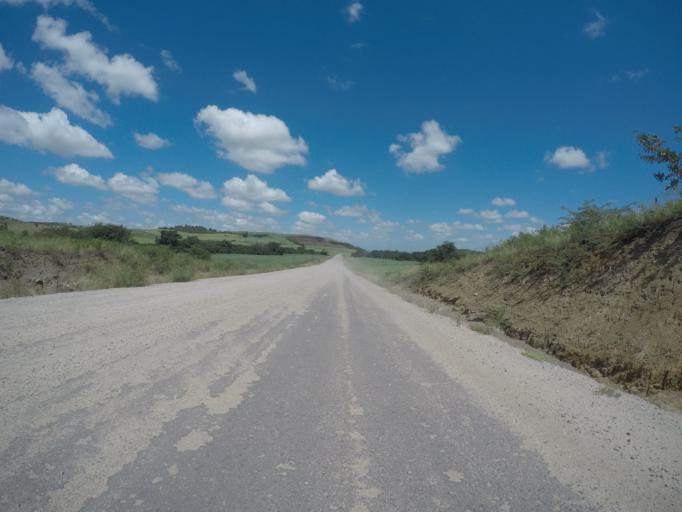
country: ZA
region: KwaZulu-Natal
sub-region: uThungulu District Municipality
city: Empangeni
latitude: -28.6413
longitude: 31.7647
